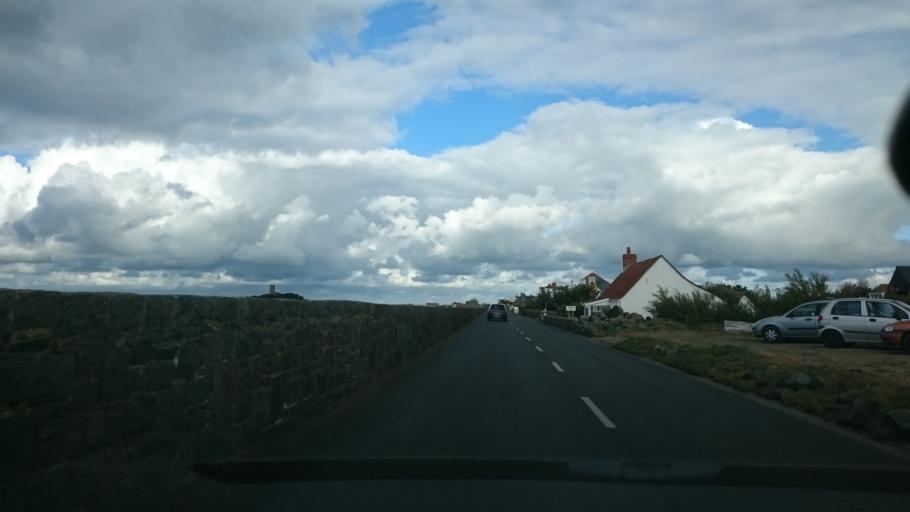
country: GG
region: St Peter Port
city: Saint Peter Port
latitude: 49.4482
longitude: -2.6495
